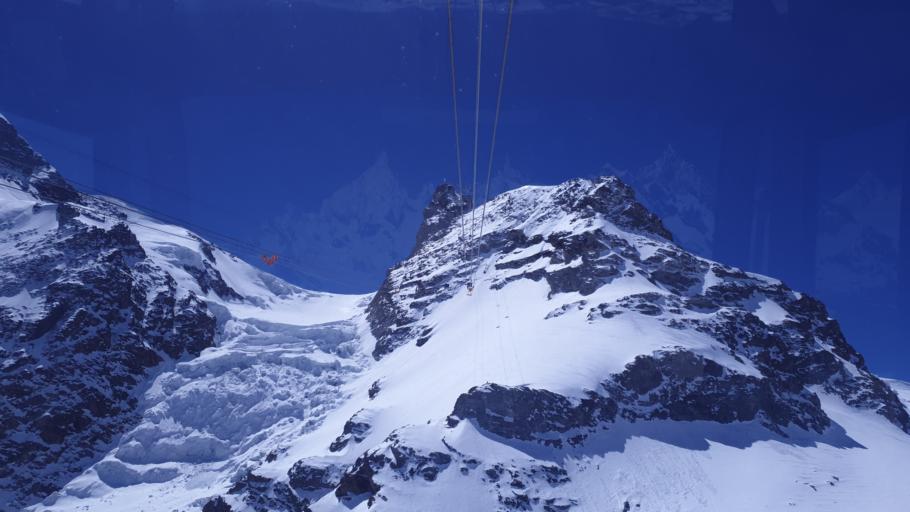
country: CH
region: Valais
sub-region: Visp District
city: Zermatt
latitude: 45.9520
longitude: 7.7259
